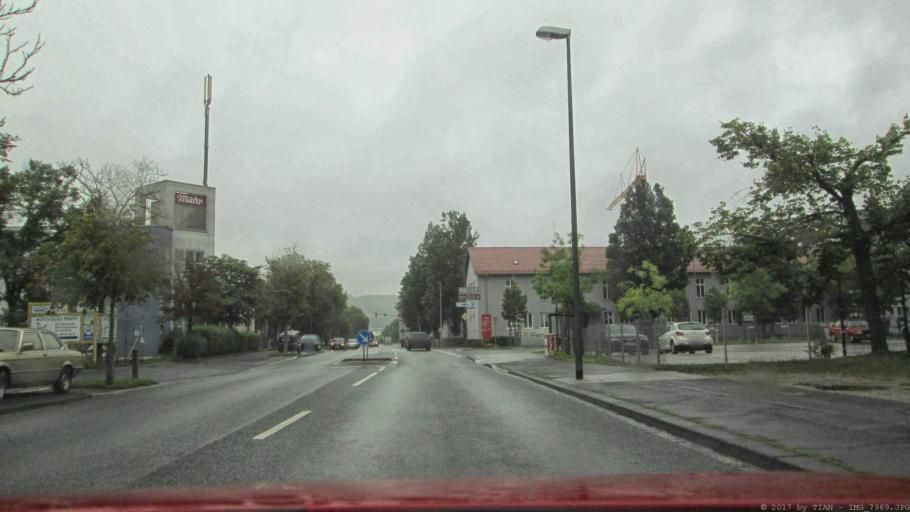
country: DE
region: Bavaria
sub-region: Regierungsbezirk Unterfranken
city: Hochberg
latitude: 49.7981
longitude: 9.9013
